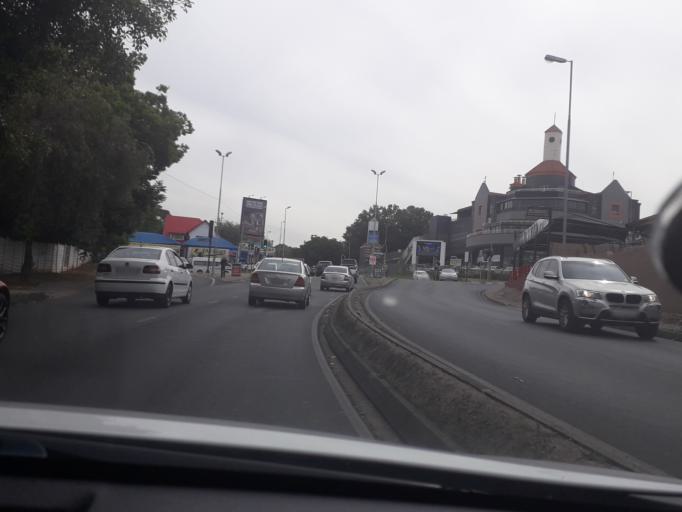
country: ZA
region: Gauteng
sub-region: City of Johannesburg Metropolitan Municipality
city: Johannesburg
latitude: -26.0987
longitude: 28.0115
